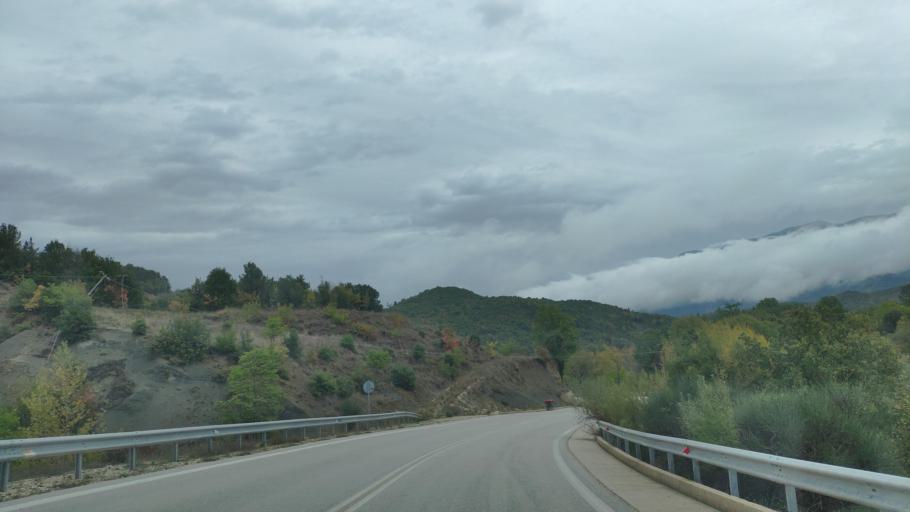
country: GR
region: Epirus
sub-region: Nomos Thesprotias
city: Paramythia
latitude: 39.5009
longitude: 20.6768
